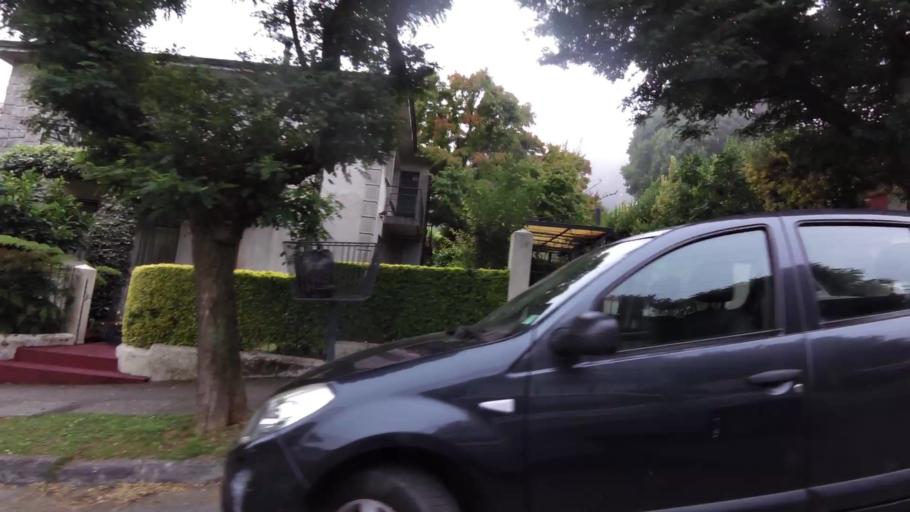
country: CL
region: Biobio
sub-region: Provincia de Concepcion
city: Concepcion
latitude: -36.8261
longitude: -73.0306
